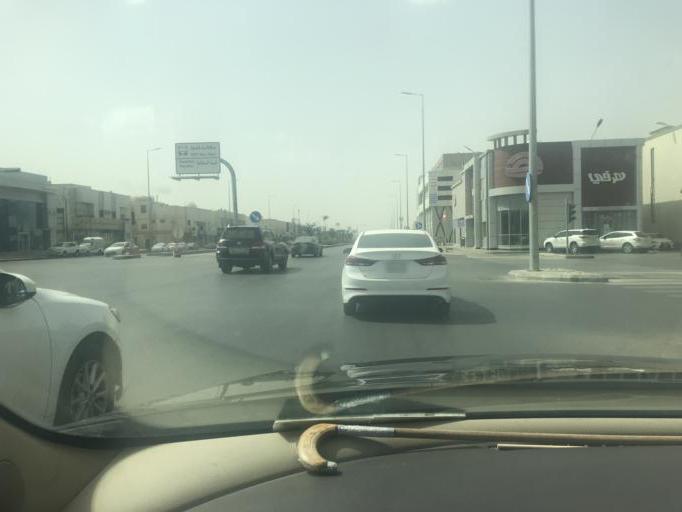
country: SA
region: Ar Riyad
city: Riyadh
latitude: 24.7374
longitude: 46.7819
